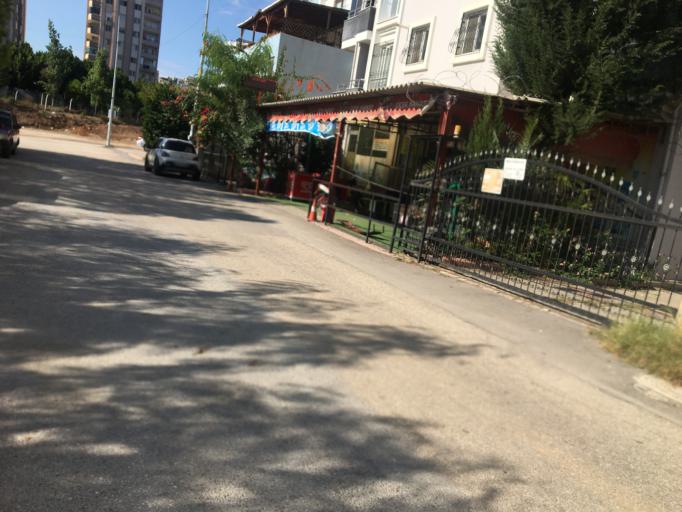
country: TR
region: Adana
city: Seyhan
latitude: 37.0291
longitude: 35.2767
